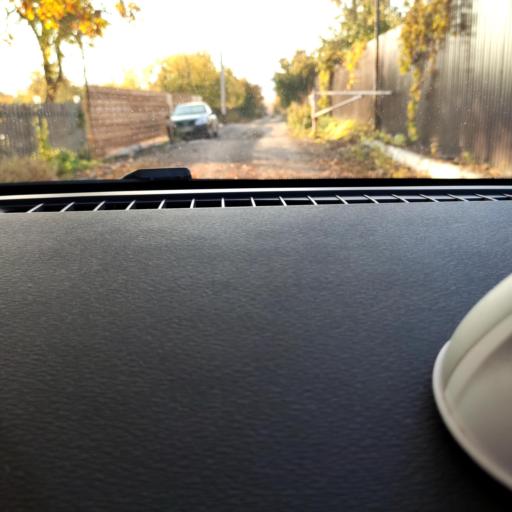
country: RU
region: Samara
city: Petra-Dubrava
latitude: 53.2590
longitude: 50.2739
